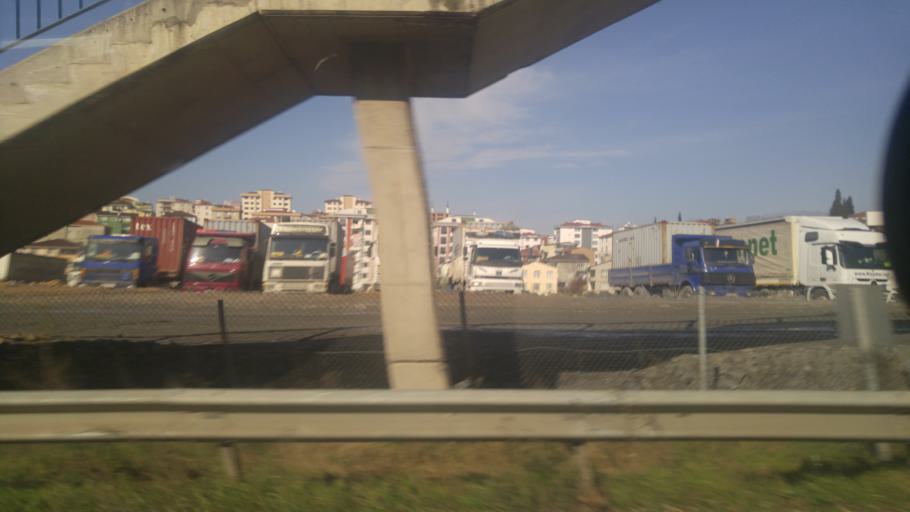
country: TR
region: Kocaeli
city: Darica
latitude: 40.8311
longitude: 29.3682
